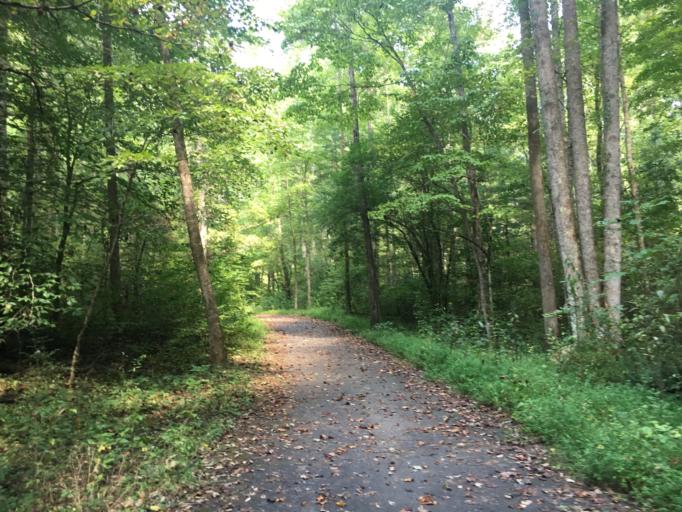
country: US
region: North Carolina
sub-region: Graham County
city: Robbinsville
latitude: 35.2761
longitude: -83.6801
